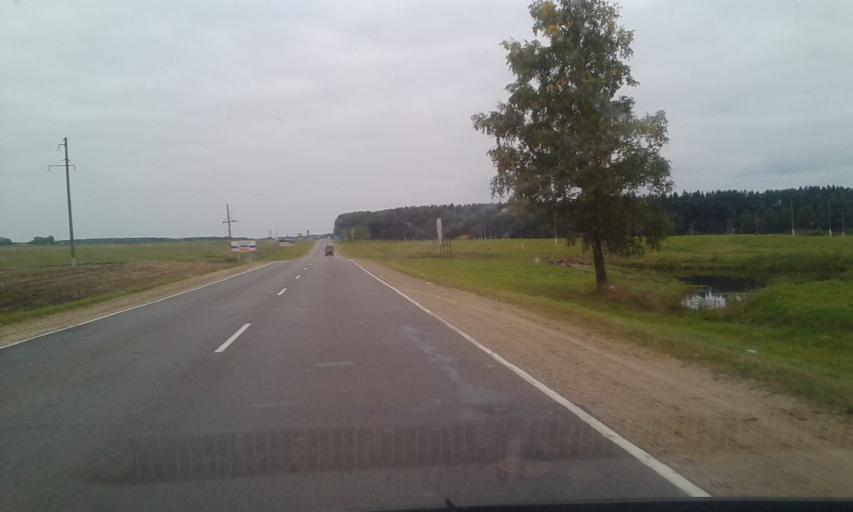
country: BY
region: Vitebsk
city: Pastavy
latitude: 55.1073
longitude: 26.8734
